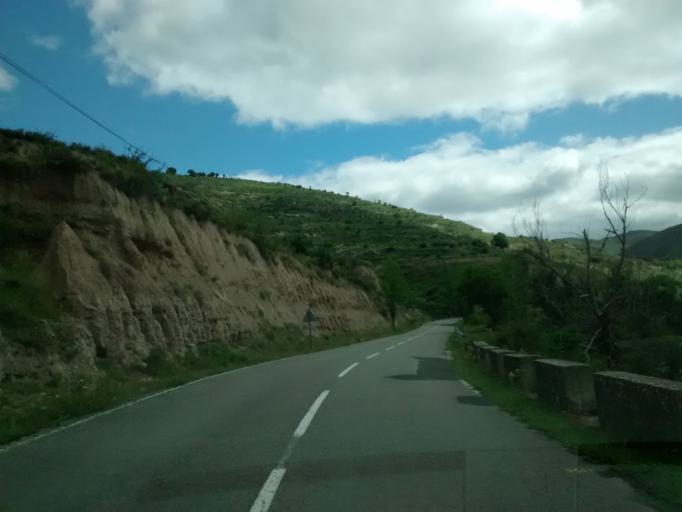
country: ES
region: La Rioja
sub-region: Provincia de La Rioja
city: Terroba
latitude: 42.2559
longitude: -2.4539
